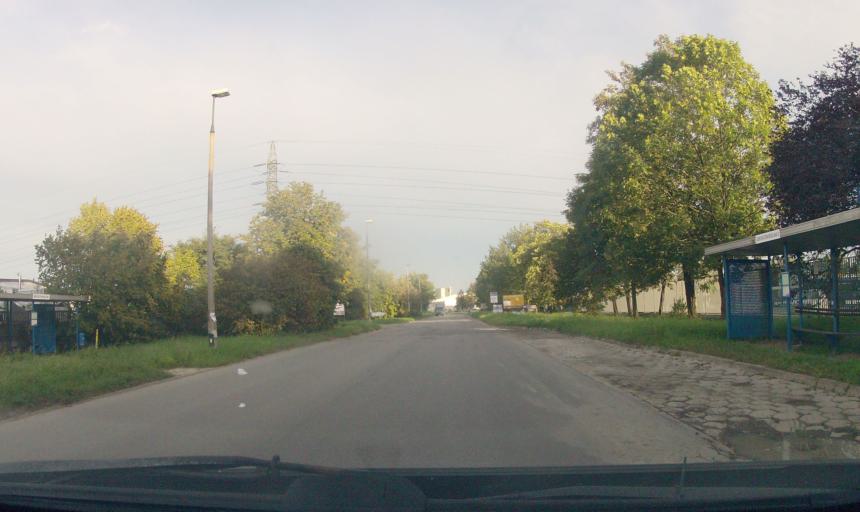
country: PL
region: Lesser Poland Voivodeship
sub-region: Powiat wielicki
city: Czarnochowice
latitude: 50.0370
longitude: 20.0095
